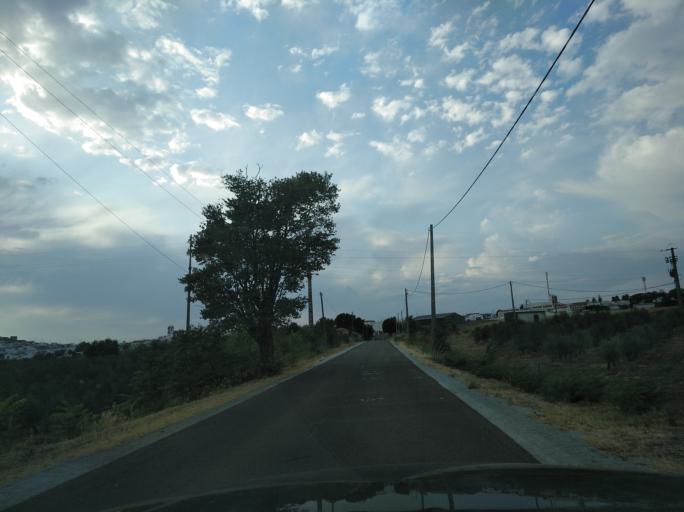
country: PT
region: Portalegre
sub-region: Campo Maior
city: Campo Maior
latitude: 39.0082
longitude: -7.0620
